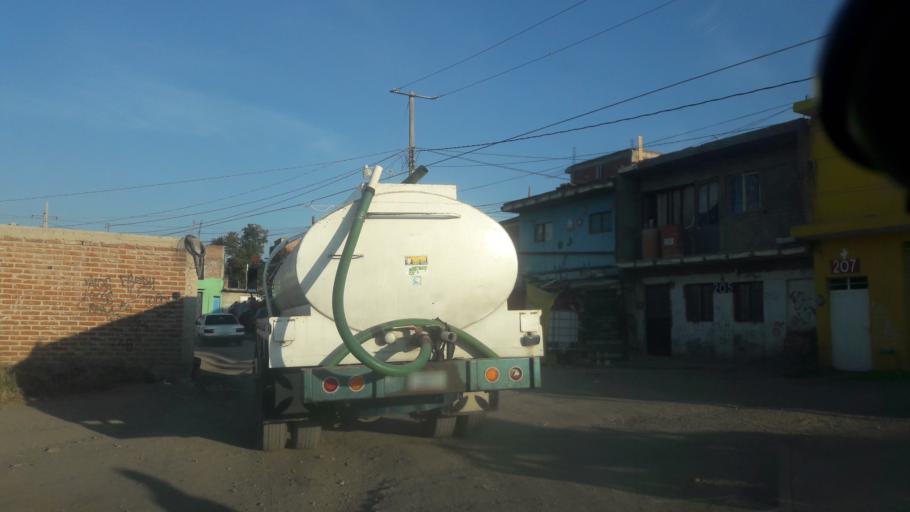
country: MX
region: Guanajuato
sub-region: Leon
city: Medina
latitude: 21.1690
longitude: -101.6382
